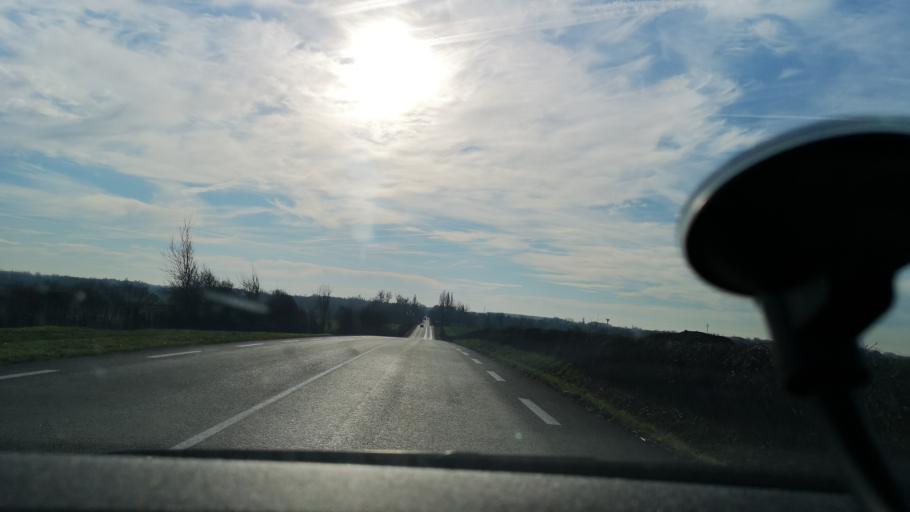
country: FR
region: Bourgogne
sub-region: Departement de la Cote-d'Or
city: Seurre
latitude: 46.9488
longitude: 5.1568
